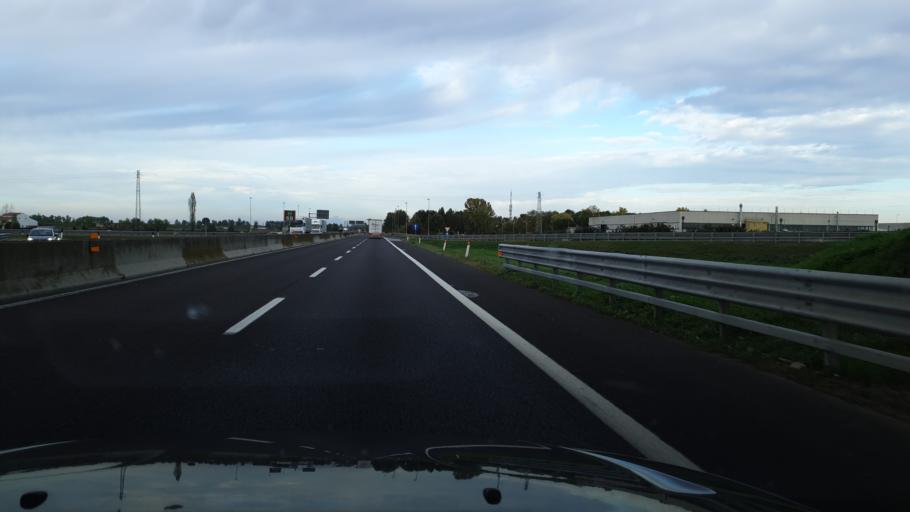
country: IT
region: Veneto
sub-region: Provincia di Rovigo
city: Grignano Polesine
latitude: 45.0815
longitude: 11.7414
